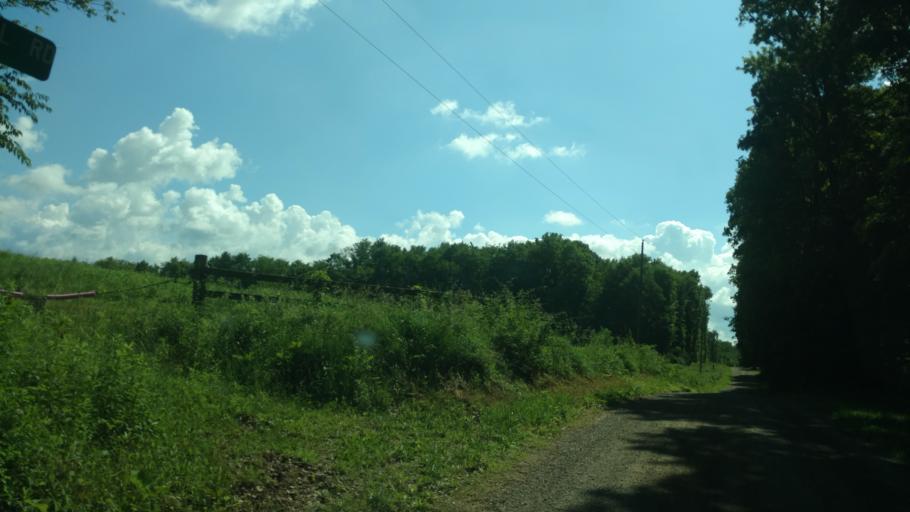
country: US
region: Ohio
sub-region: Knox County
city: Danville
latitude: 40.5033
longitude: -82.2732
